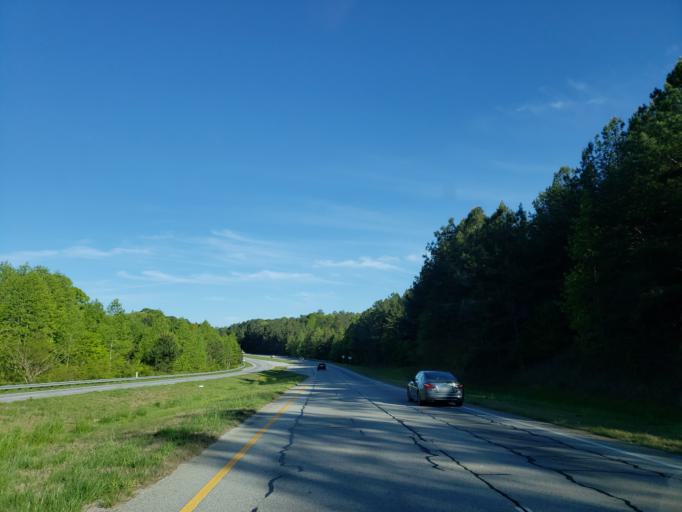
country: US
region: Georgia
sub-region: Paulding County
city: Dallas
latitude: 33.9172
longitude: -84.9262
